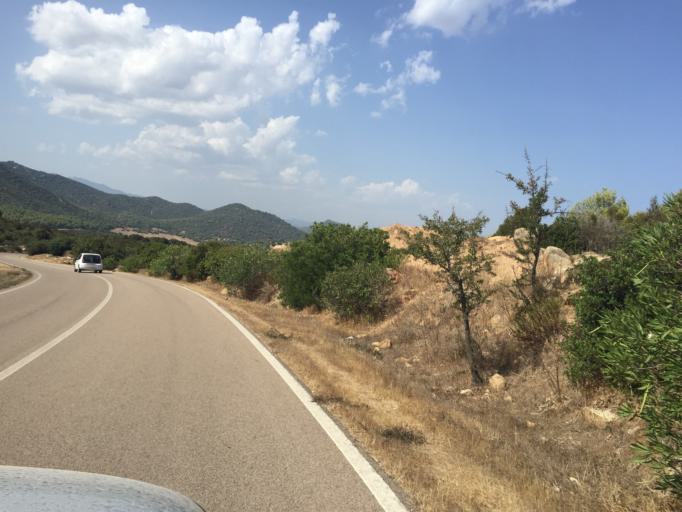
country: IT
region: Sardinia
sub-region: Provincia di Cagliari
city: Villasimius
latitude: 39.1662
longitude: 9.5622
